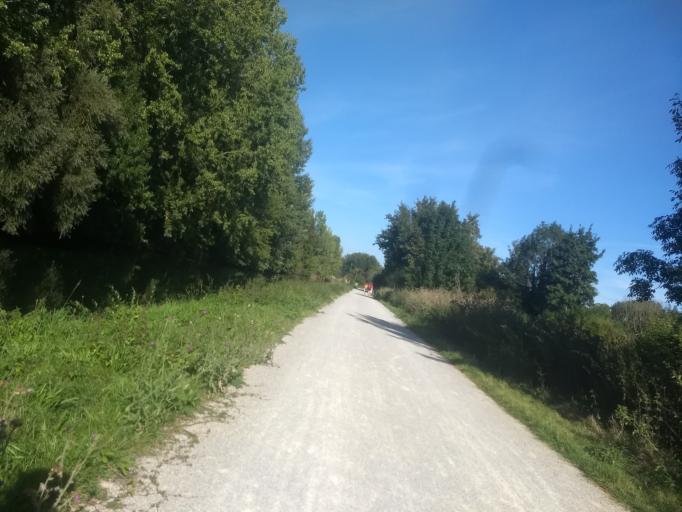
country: FR
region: Nord-Pas-de-Calais
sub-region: Departement du Pas-de-Calais
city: Fampoux
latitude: 50.2991
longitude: 2.8724
